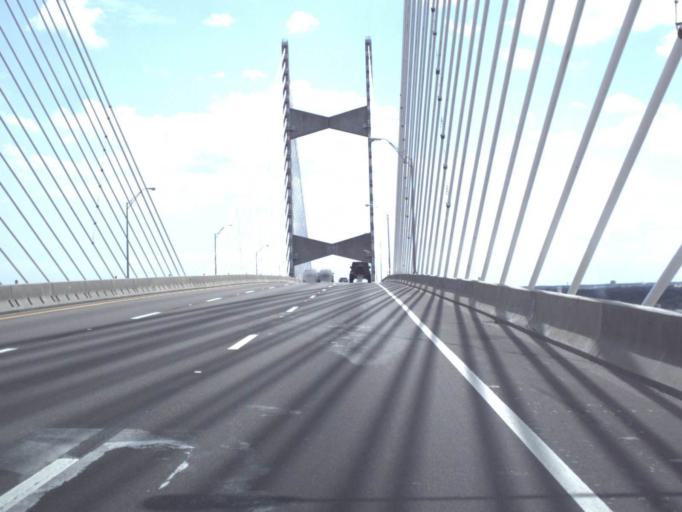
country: US
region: Florida
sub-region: Duval County
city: Jacksonville
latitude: 30.3857
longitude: -81.5576
